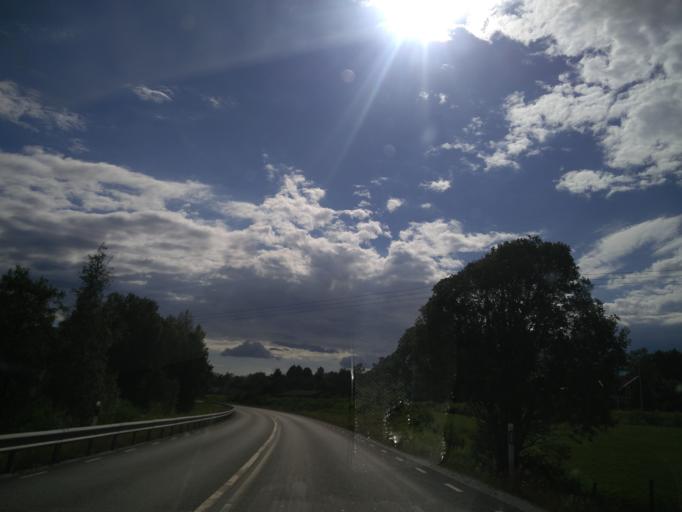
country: SE
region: Vaermland
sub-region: Filipstads Kommun
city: Filipstad
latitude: 59.7517
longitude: 14.2412
